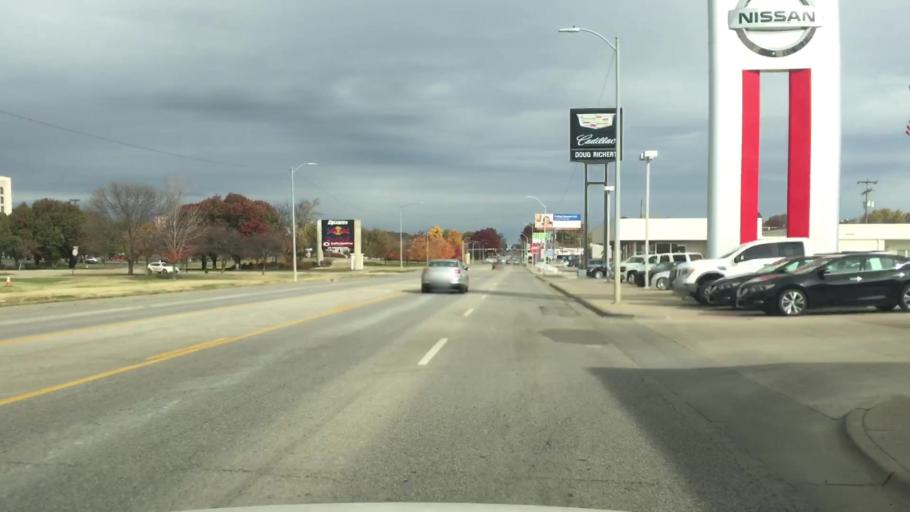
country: US
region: Kansas
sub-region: Shawnee County
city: Topeka
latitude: 39.0332
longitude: -95.6828
